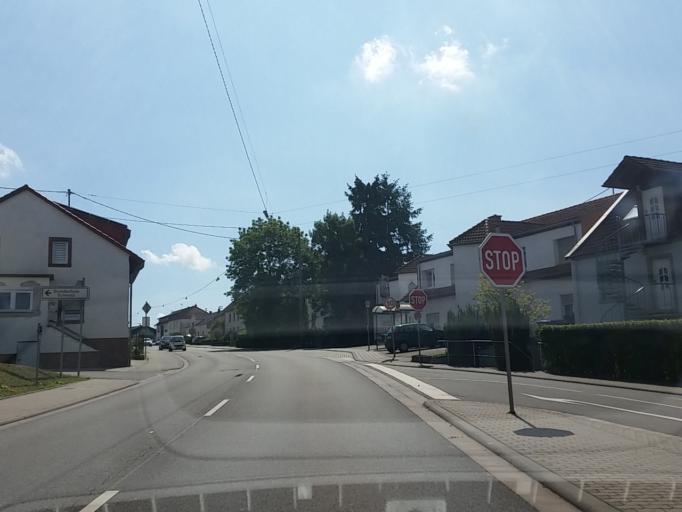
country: DE
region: Saarland
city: Schmelz
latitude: 49.4405
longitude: 6.8611
